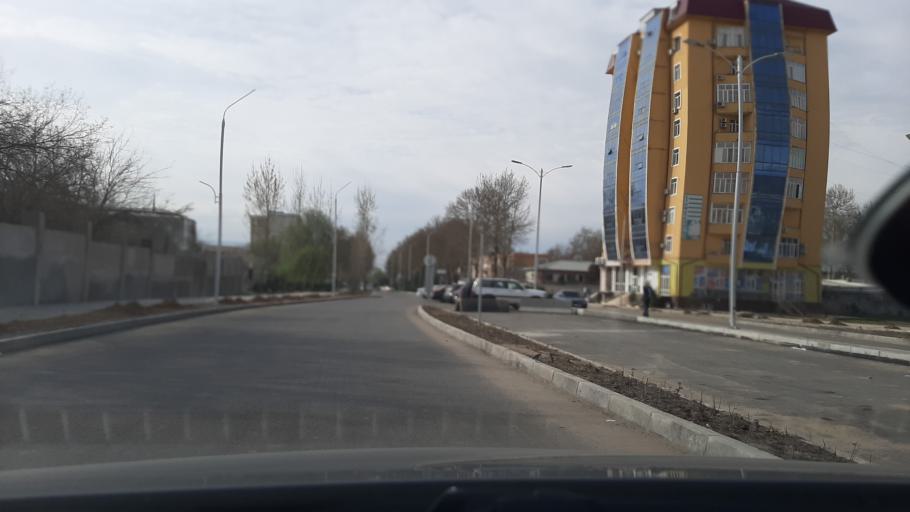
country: TJ
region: Dushanbe
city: Dushanbe
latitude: 38.5823
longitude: 68.7492
